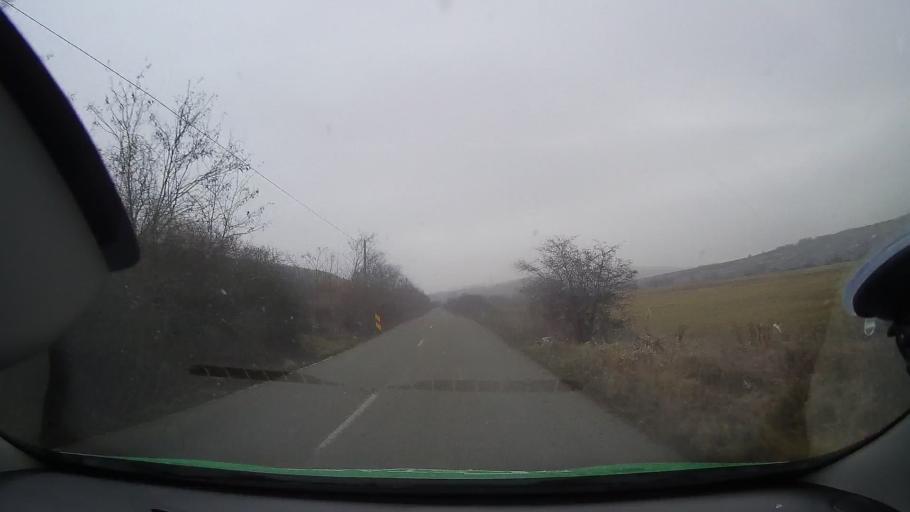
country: RO
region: Alba
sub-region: Comuna Farau
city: Farau
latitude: 46.3355
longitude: 23.9607
